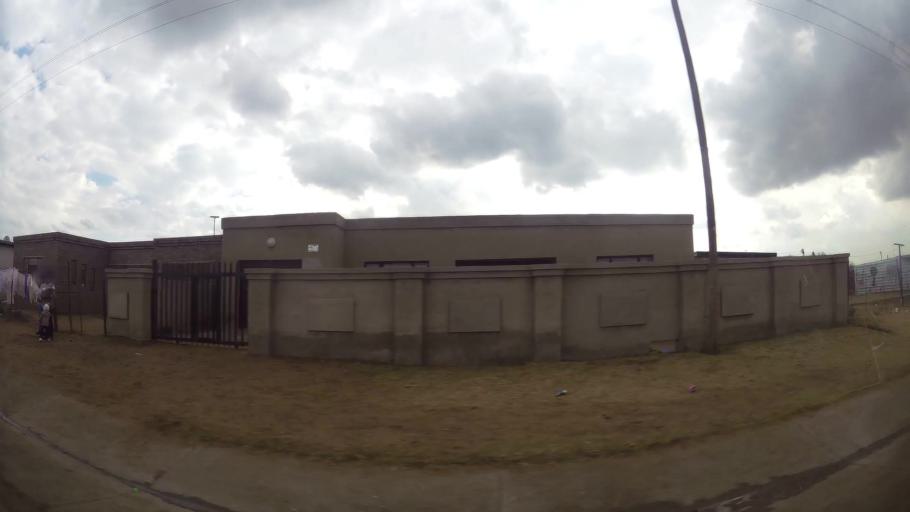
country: ZA
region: Orange Free State
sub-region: Fezile Dabi District Municipality
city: Sasolburg
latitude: -26.8544
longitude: 27.8595
